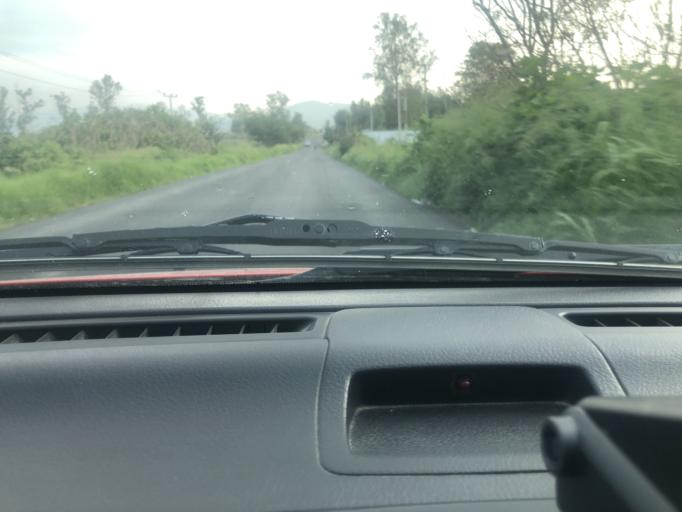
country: MX
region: Jalisco
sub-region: San Pedro Tlaquepaque
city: Paseo del Prado
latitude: 20.5718
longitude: -103.4063
